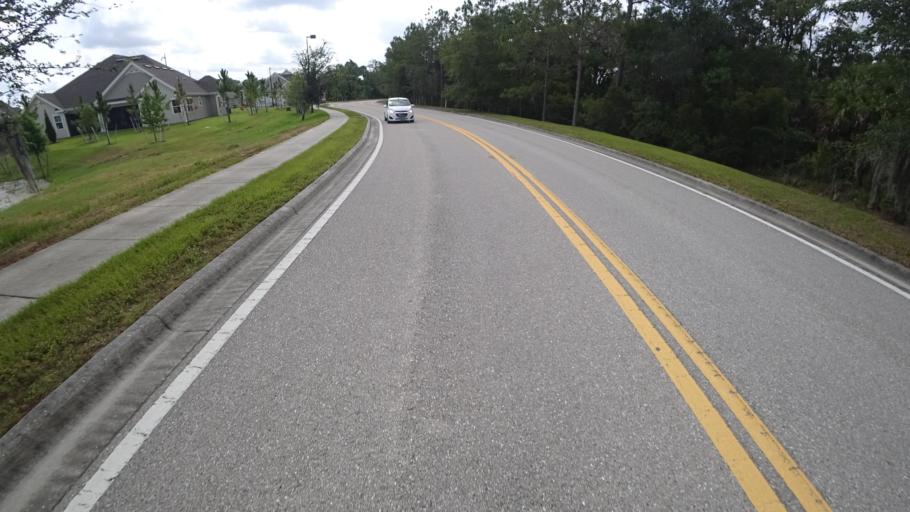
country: US
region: Florida
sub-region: Sarasota County
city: Desoto Lakes
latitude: 27.4205
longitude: -82.4562
